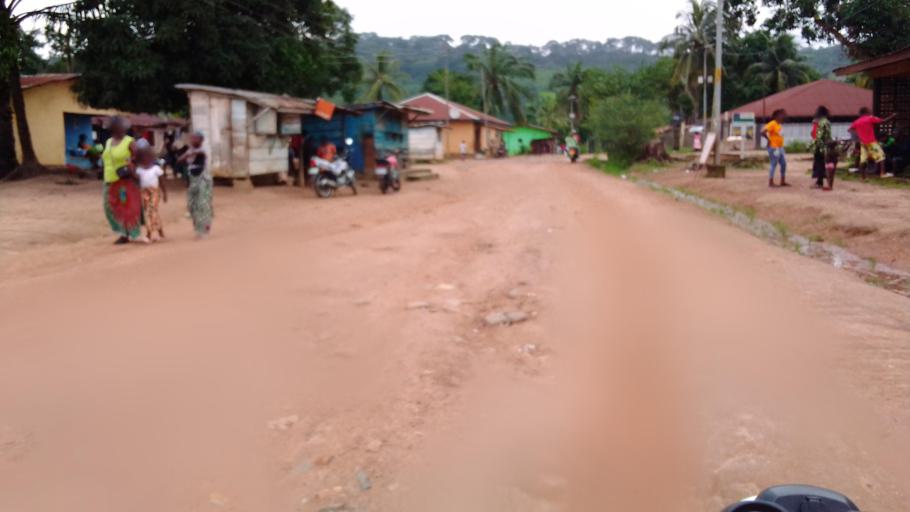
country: SL
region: Eastern Province
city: Kenema
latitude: 7.8591
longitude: -11.2048
